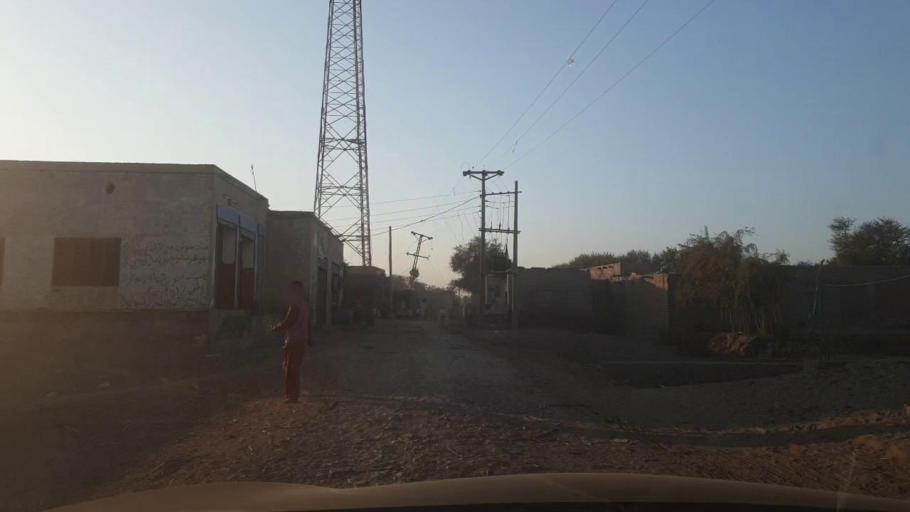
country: PK
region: Sindh
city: Ubauro
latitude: 28.1712
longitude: 69.6023
